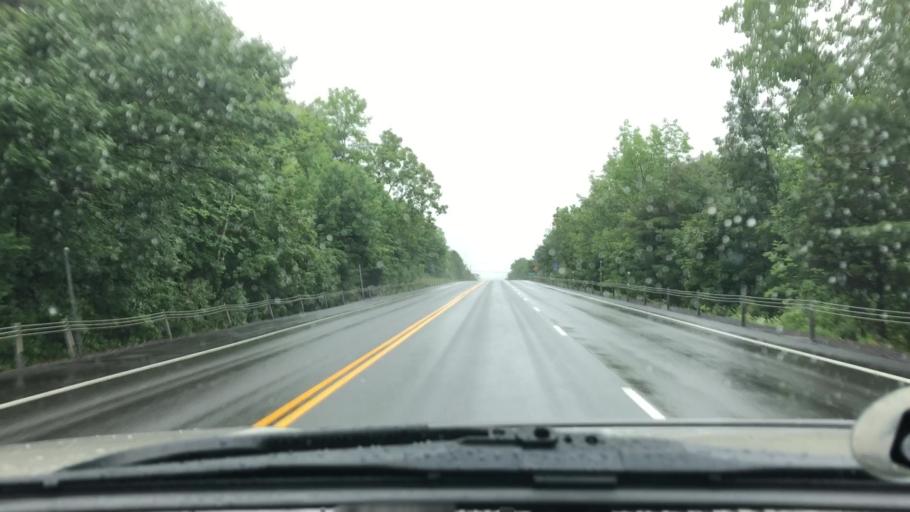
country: US
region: New York
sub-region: Greene County
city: Cairo
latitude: 42.3072
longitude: -74.0495
